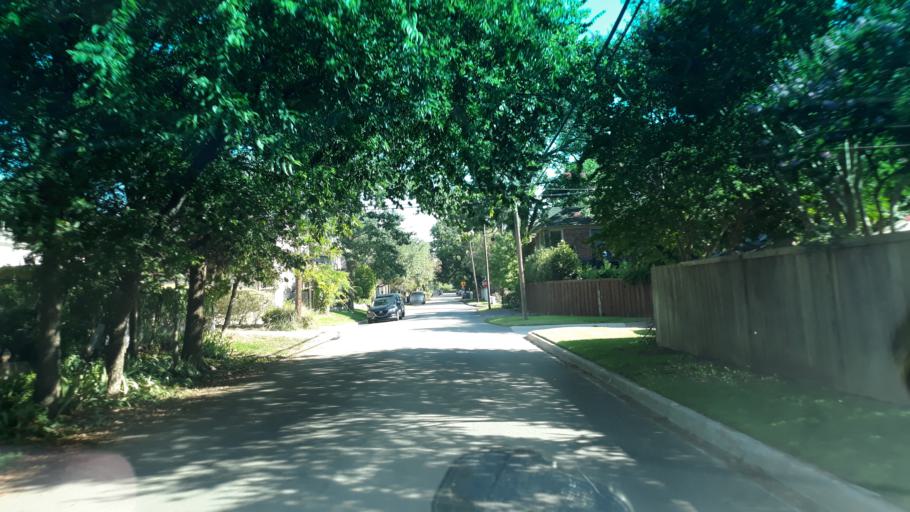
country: US
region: Texas
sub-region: Dallas County
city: Highland Park
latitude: 32.8188
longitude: -96.7587
